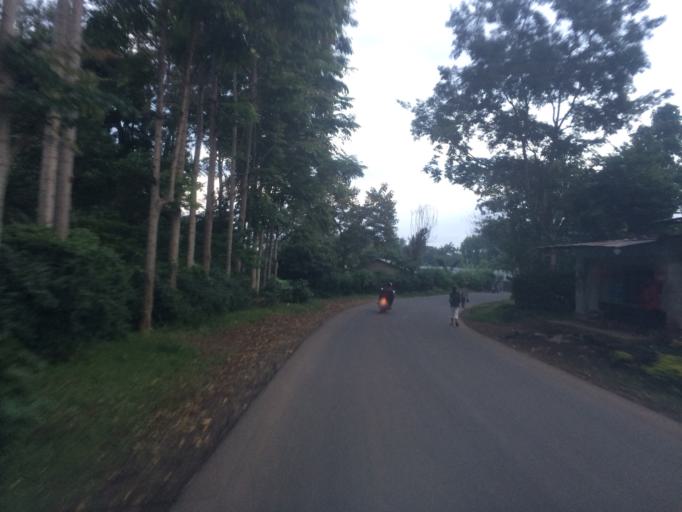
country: TZ
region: Arusha
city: Nkoaranga
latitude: -3.3623
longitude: 36.8160
